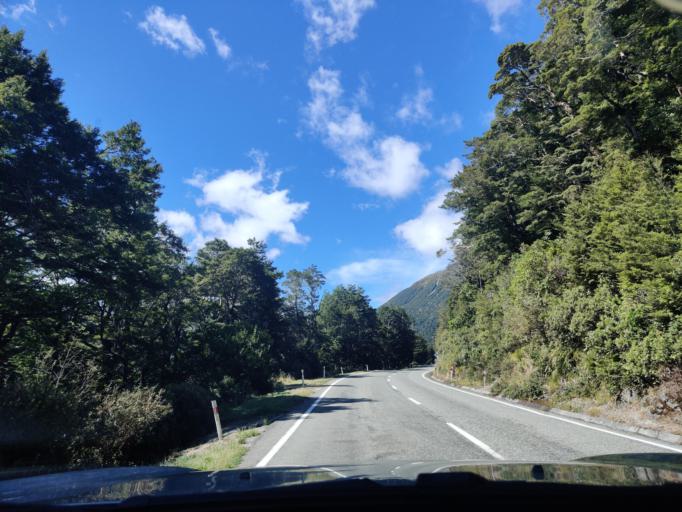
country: NZ
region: Canterbury
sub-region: Hurunui District
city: Amberley
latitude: -42.3748
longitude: 172.3898
